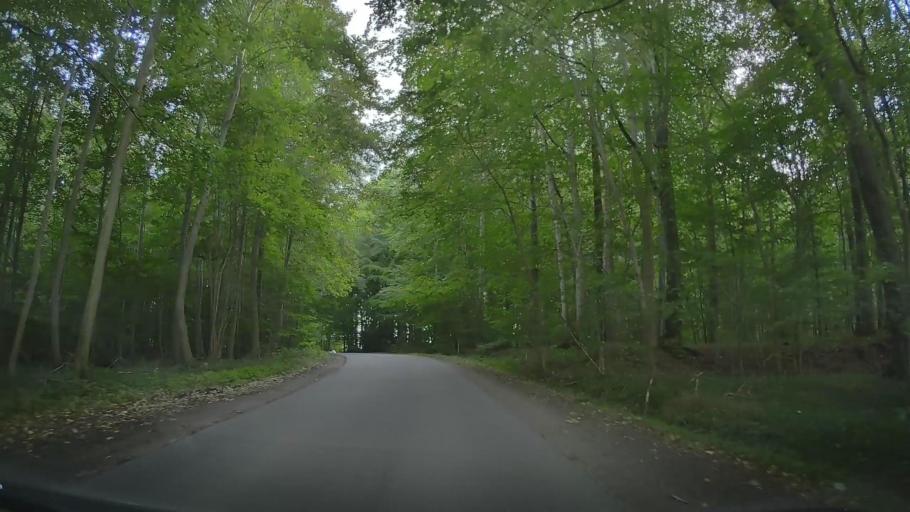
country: DE
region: Schleswig-Holstein
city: Steinberg
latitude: 54.7865
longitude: 9.7793
